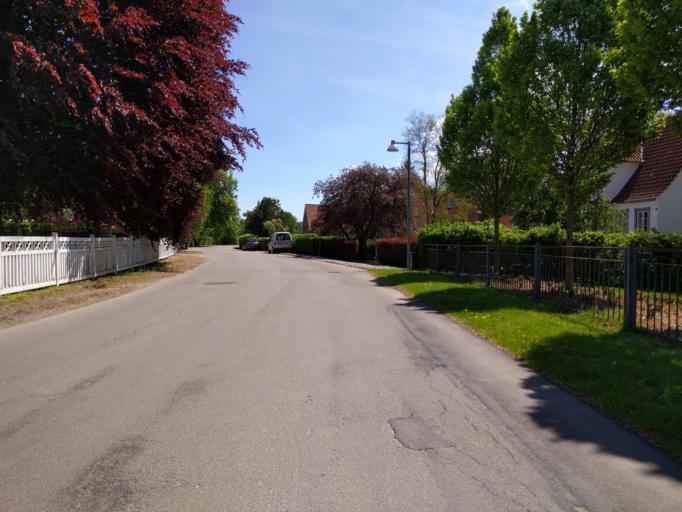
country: DK
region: Zealand
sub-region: Guldborgsund Kommune
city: Nykobing Falster
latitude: 54.7447
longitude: 11.9546
